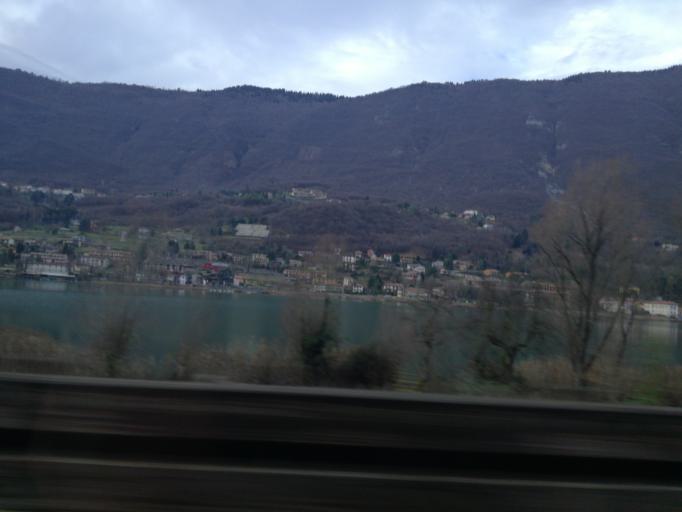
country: IT
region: Lombardy
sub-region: Provincia di Bergamo
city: Ranzanico
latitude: 45.7852
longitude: 9.9519
